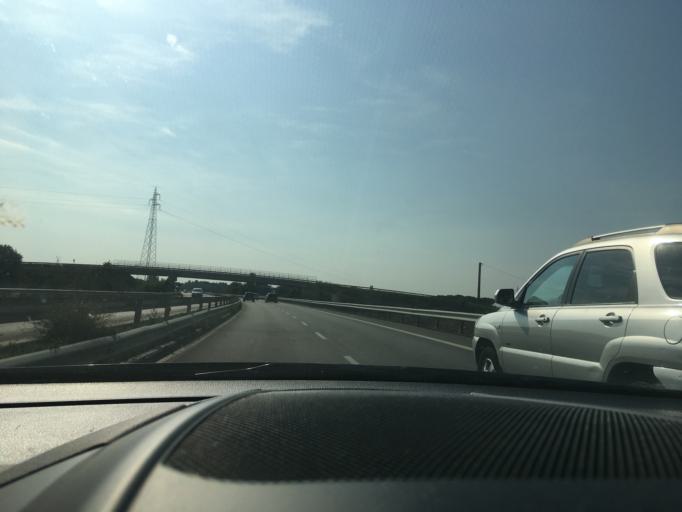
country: IT
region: Emilia-Romagna
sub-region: Provincia di Rimini
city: Bellaria-Igea Marina
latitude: 44.1160
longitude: 12.4757
